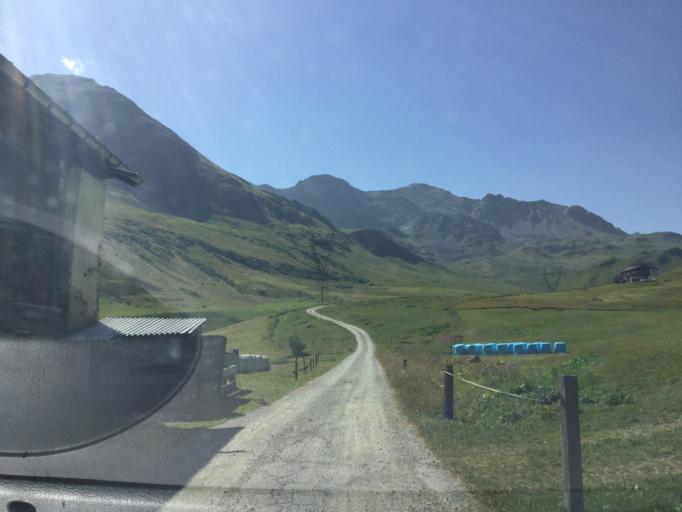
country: CH
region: Grisons
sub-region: Maloja District
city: Silvaplana
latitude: 46.4585
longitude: 9.6564
